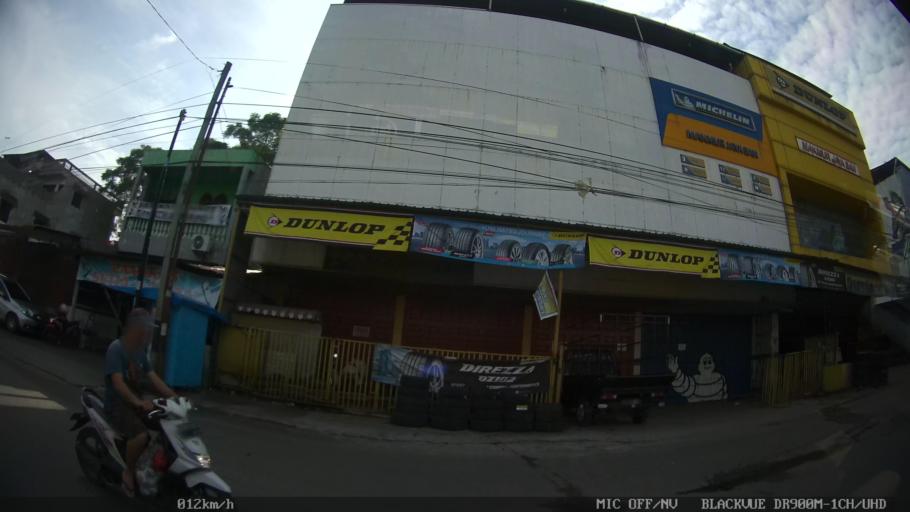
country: ID
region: North Sumatra
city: Medan
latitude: 3.5703
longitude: 98.6426
